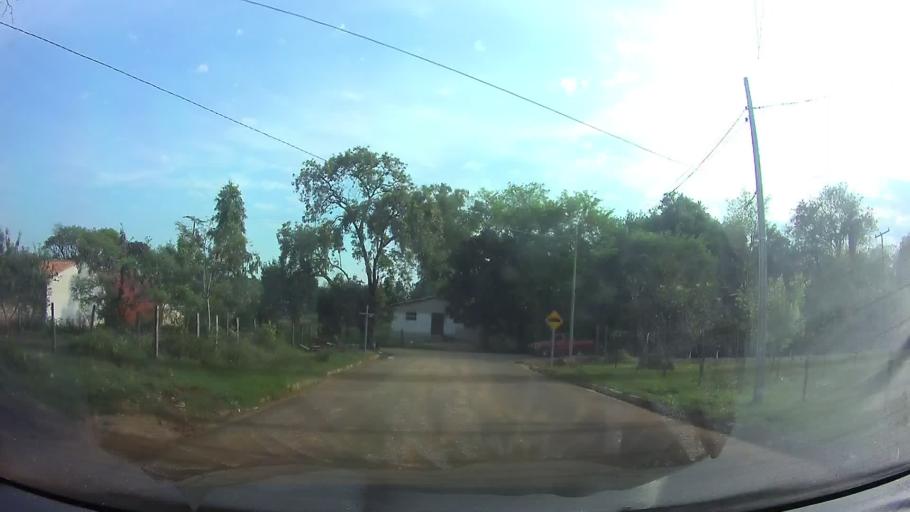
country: PY
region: Central
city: San Lorenzo
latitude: -25.2558
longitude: -57.4798
